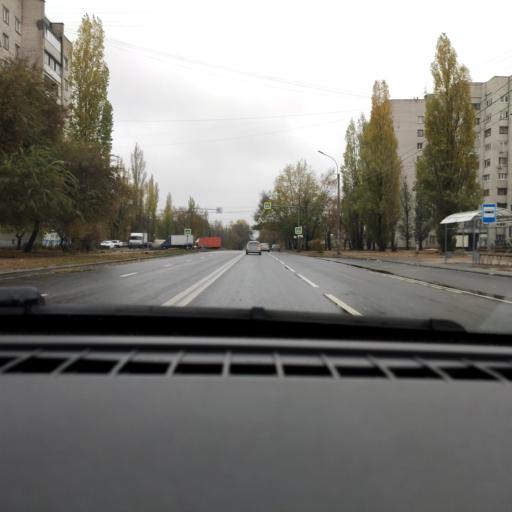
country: RU
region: Voronezj
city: Maslovka
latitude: 51.5964
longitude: 39.2438
